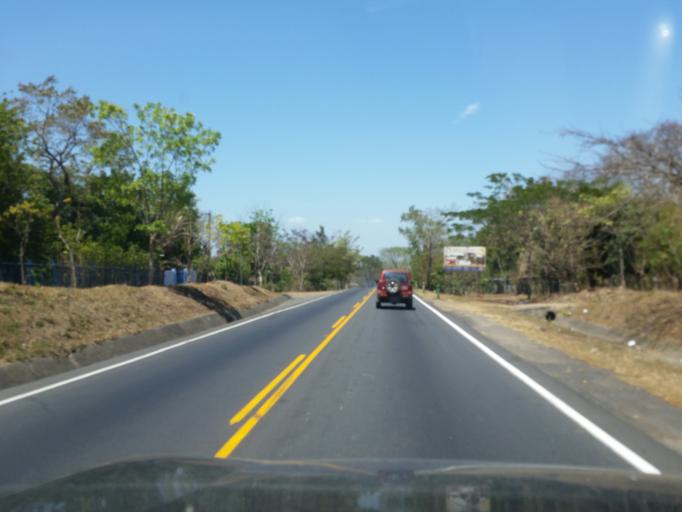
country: NI
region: Masaya
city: Masaya
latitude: 11.9495
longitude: -86.0918
